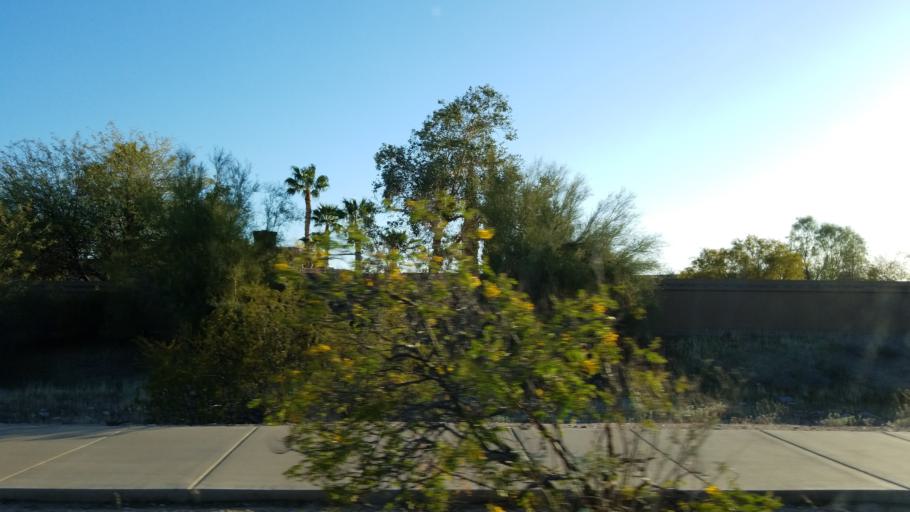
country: US
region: Arizona
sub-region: Maricopa County
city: Scottsdale
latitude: 33.5996
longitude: -111.8468
